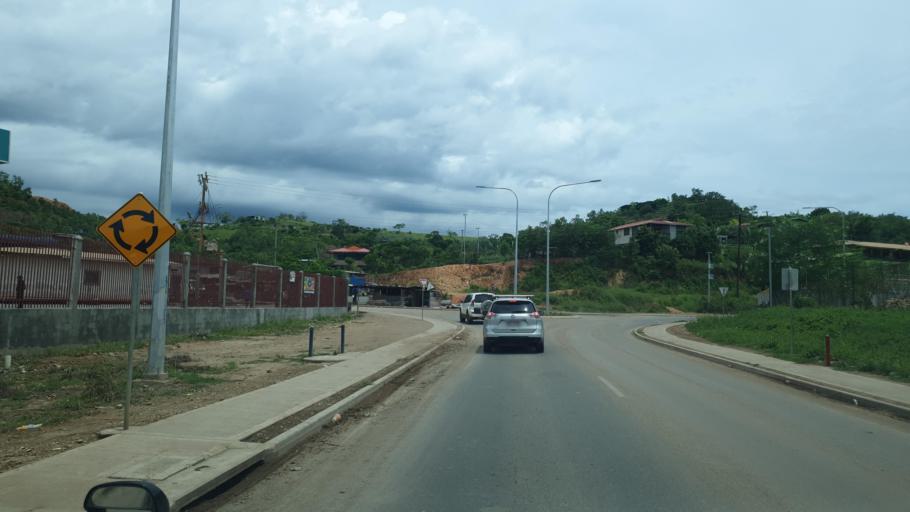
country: PG
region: National Capital
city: Port Moresby
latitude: -9.5099
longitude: 147.2417
